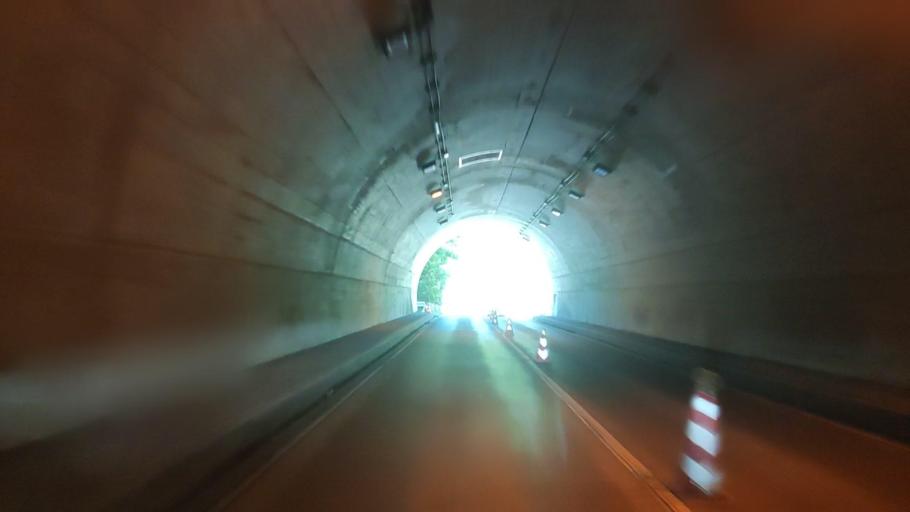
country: JP
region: Nara
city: Yoshino-cho
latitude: 34.2846
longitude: 136.0040
